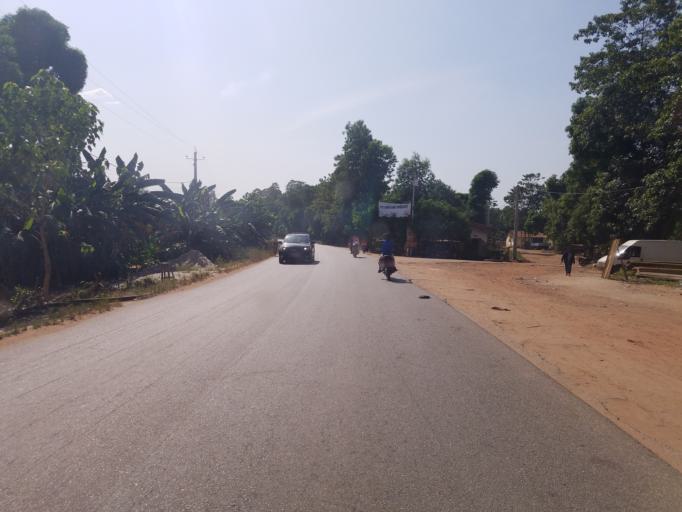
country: GN
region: Boke
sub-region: Fria
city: Fria
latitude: 10.0812
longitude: -13.6971
